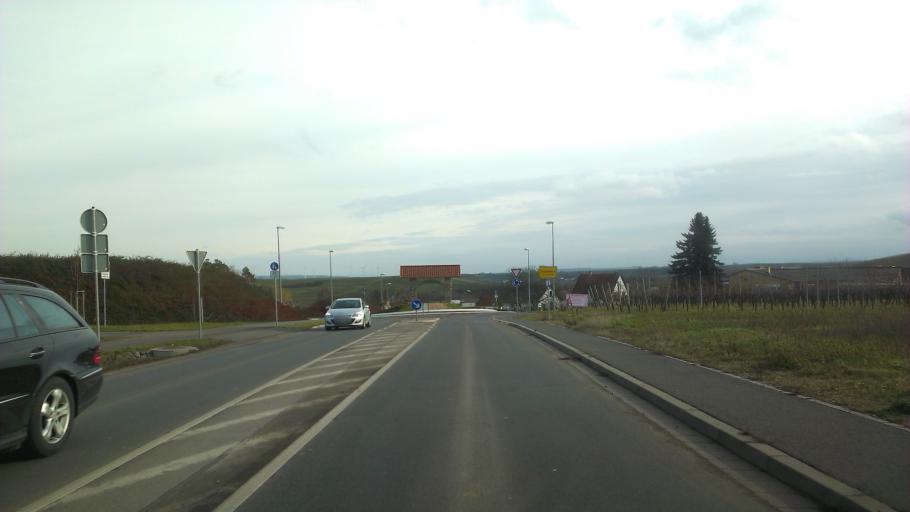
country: DE
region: Rheinland-Pfalz
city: Hackenheim
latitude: 49.8266
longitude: 7.8952
